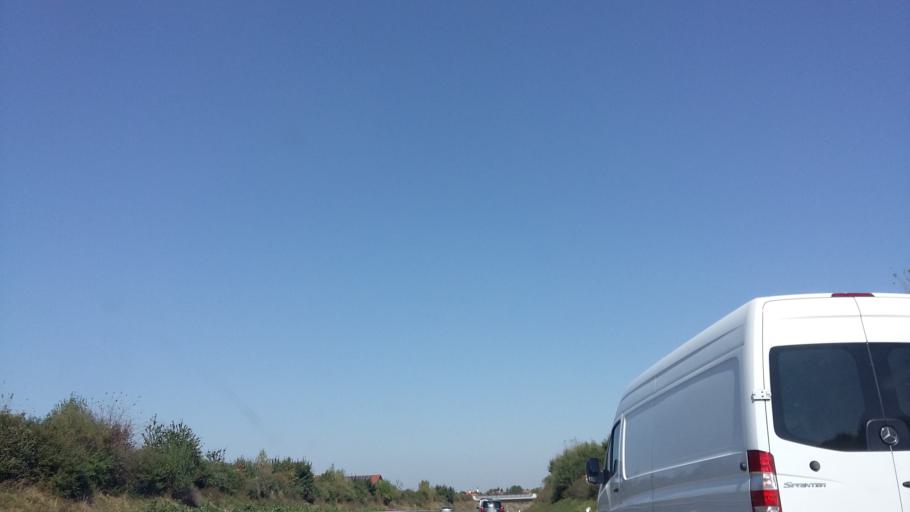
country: DE
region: Bavaria
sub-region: Swabia
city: Klosterlechfeld
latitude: 48.1411
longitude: 10.8315
